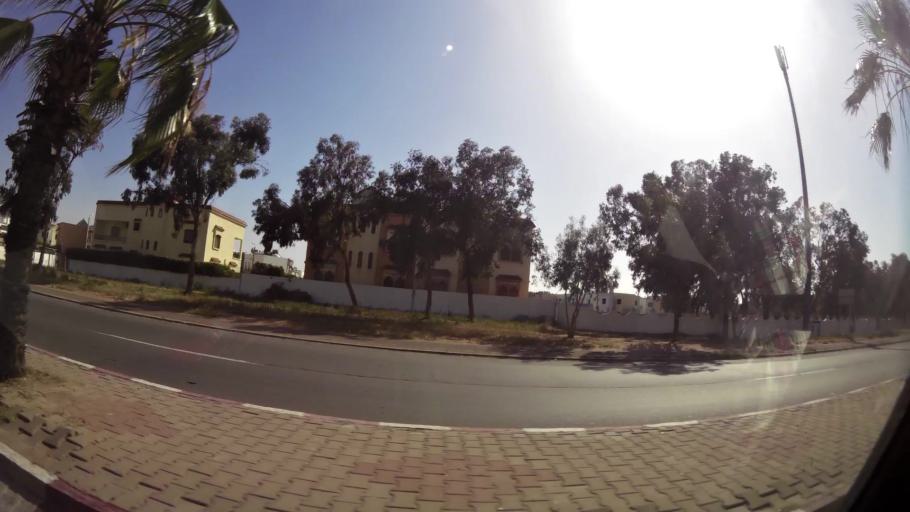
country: MA
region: Oued ed Dahab-Lagouira
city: Dakhla
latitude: 30.3785
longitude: -9.5611
